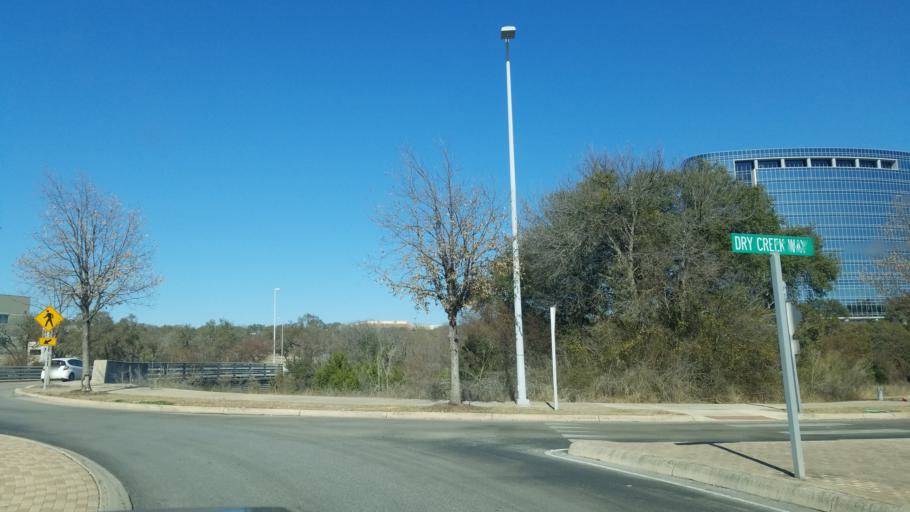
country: US
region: Texas
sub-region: Bexar County
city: Hollywood Park
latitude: 29.6159
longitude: -98.4629
